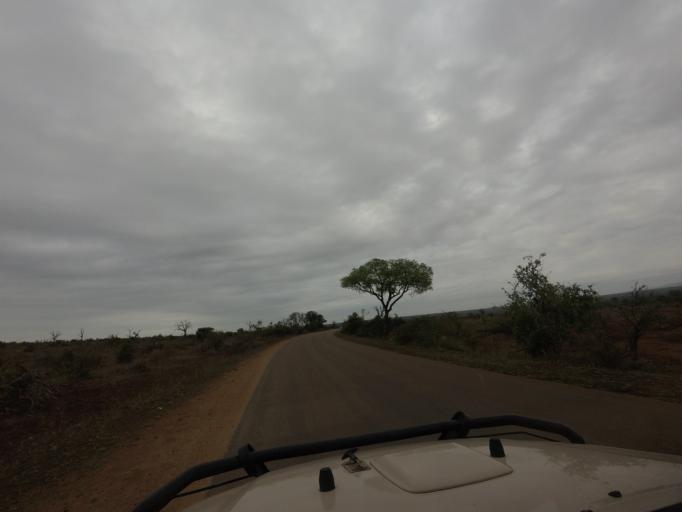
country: ZA
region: Mpumalanga
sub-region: Ehlanzeni District
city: Komatipoort
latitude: -25.3494
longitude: 31.8843
